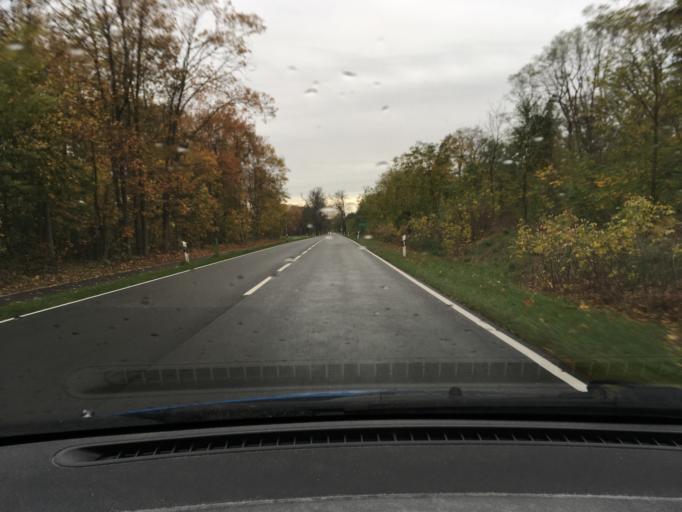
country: DE
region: Saxony-Anhalt
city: Rodleben
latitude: 51.9155
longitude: 12.1827
